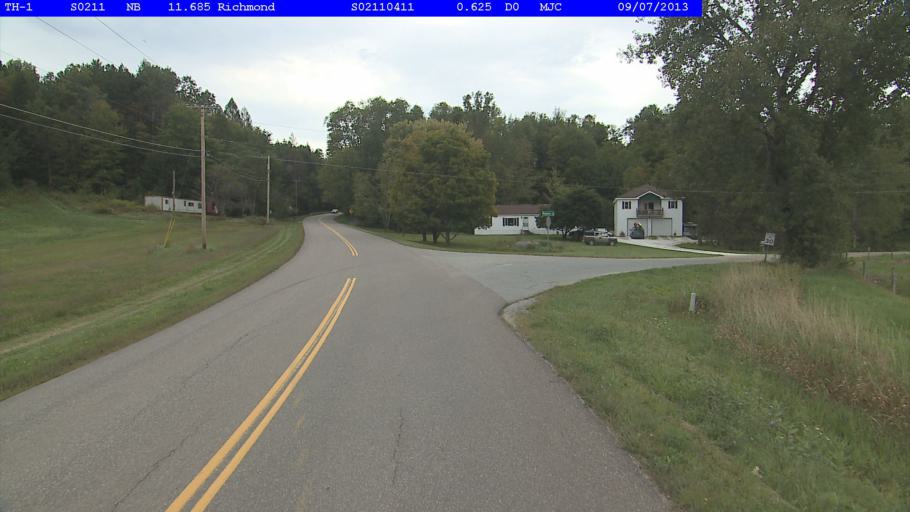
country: US
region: Vermont
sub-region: Chittenden County
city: Williston
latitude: 44.3622
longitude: -72.9938
